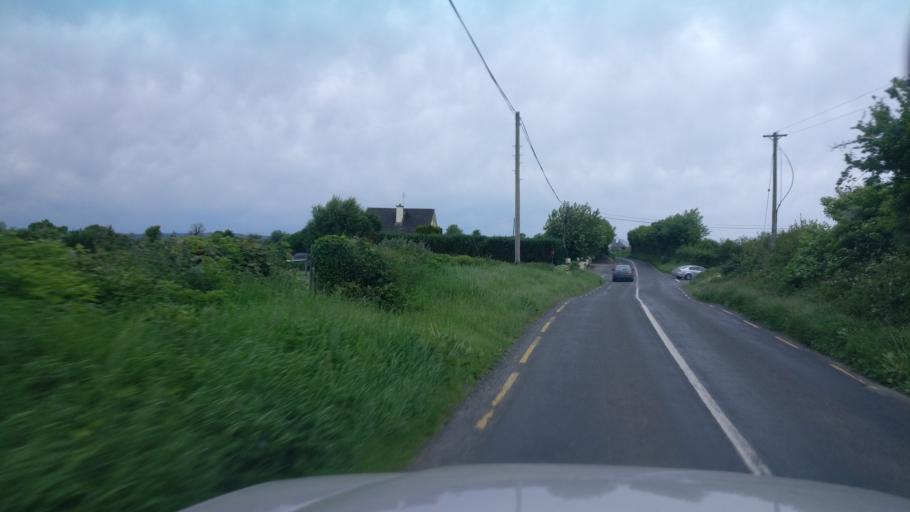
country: IE
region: Connaught
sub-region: County Galway
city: Portumna
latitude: 53.1229
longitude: -8.3301
